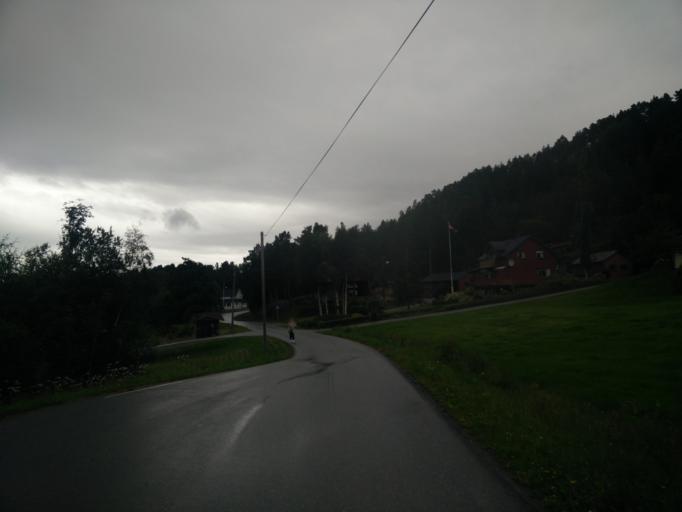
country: NO
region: More og Romsdal
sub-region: Kristiansund
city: Rensvik
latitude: 63.0195
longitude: 7.8999
